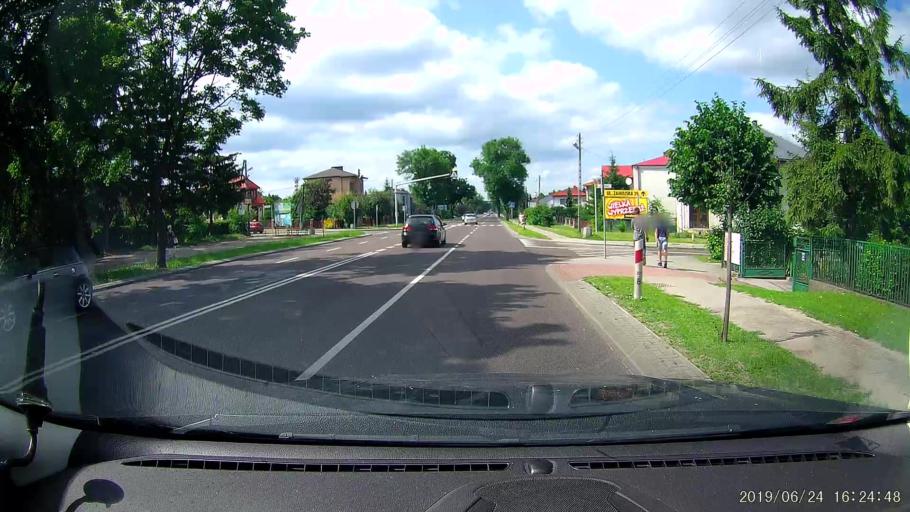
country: PL
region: Lublin Voivodeship
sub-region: Powiat tomaszowski
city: Tomaszow Lubelski
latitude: 50.4383
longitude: 23.4193
